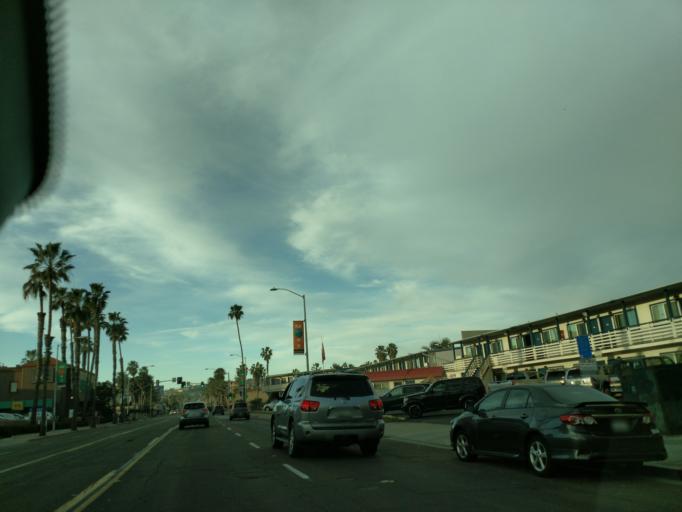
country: US
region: California
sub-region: San Diego County
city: La Jolla
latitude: 32.7916
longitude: -117.2539
